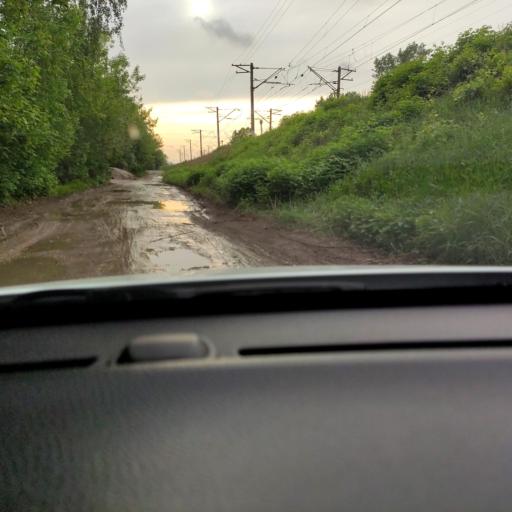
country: RU
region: Tatarstan
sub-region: Gorod Kazan'
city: Kazan
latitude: 55.8465
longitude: 49.1724
